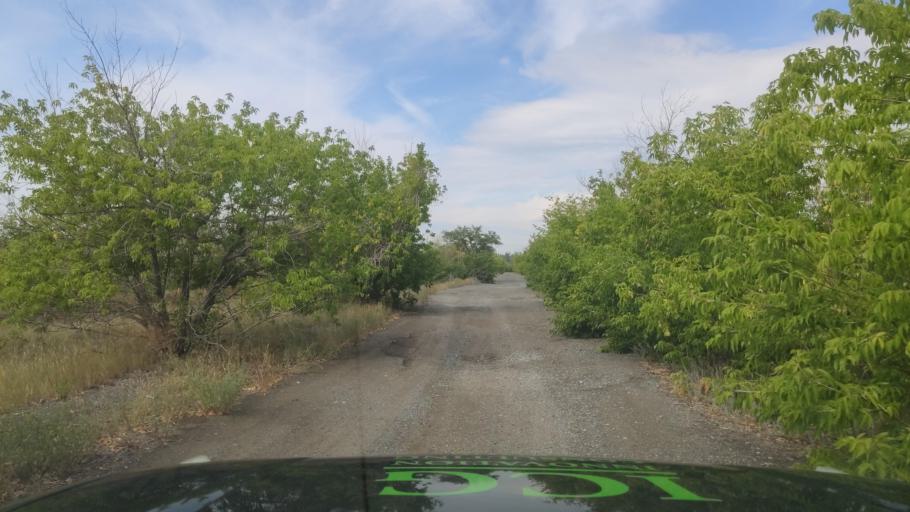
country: KZ
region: Pavlodar
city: Leninskiy
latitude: 52.4974
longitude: 76.8288
